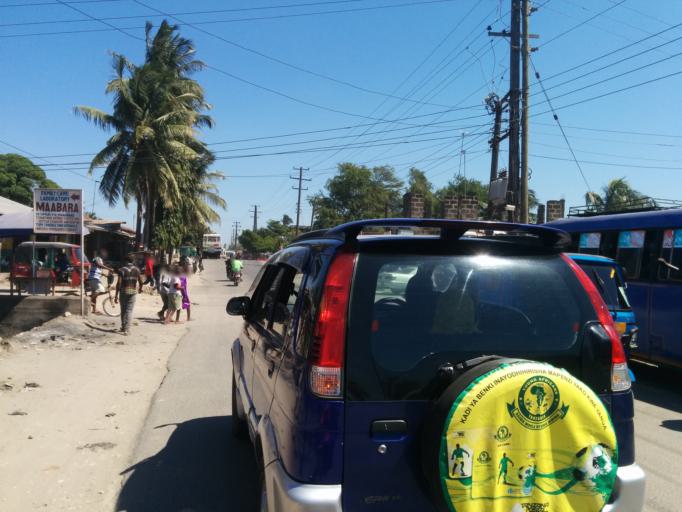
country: TZ
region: Dar es Salaam
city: Magomeni
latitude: -6.7914
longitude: 39.2431
